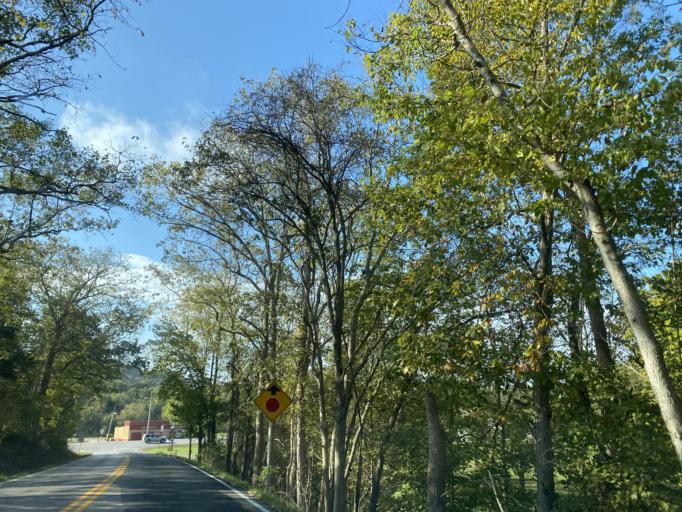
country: US
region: Kentucky
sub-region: Pendleton County
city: Falmouth
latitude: 38.6784
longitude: -84.3229
